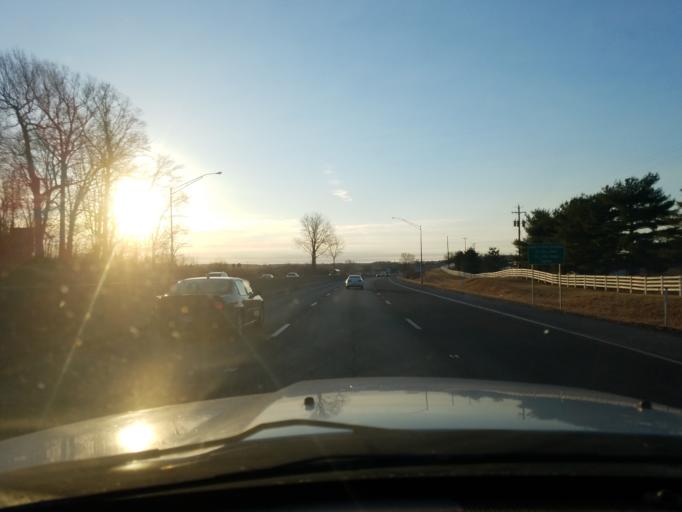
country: US
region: Kentucky
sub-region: Henderson County
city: Henderson
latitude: 37.8548
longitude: -87.5710
